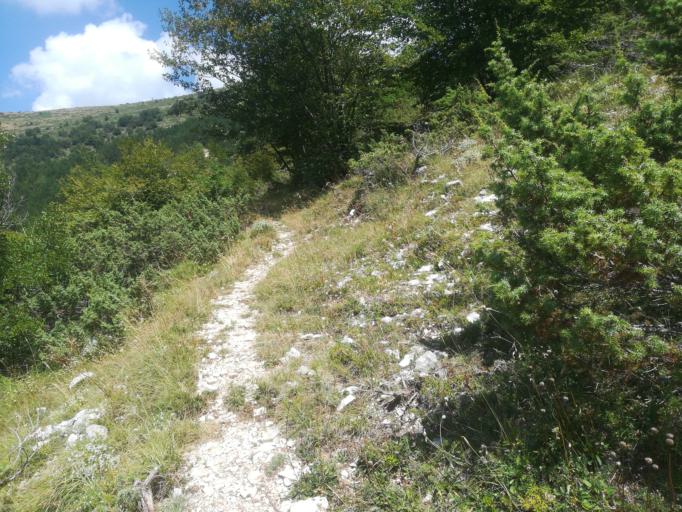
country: IT
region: Umbria
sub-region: Provincia di Perugia
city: Scheggino
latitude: 42.6723
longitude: 12.8553
